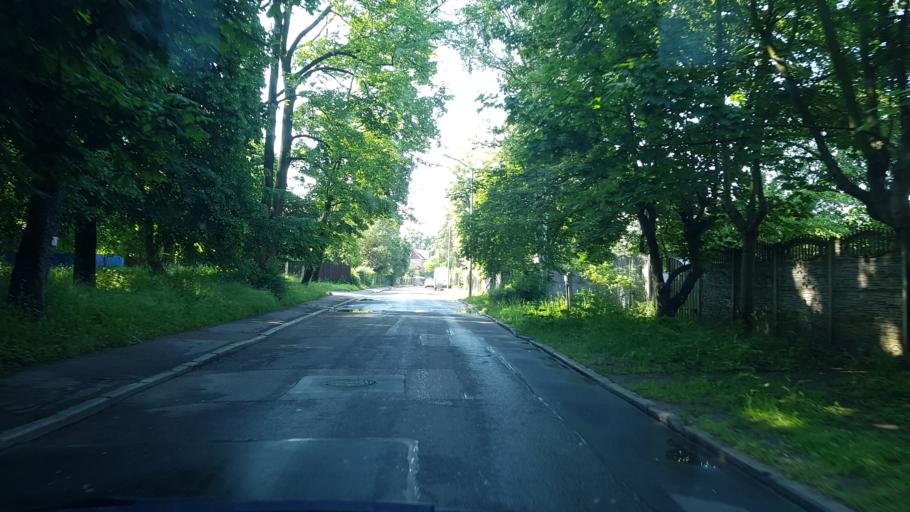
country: RU
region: Kaliningrad
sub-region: Gorod Kaliningrad
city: Kaliningrad
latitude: 54.7211
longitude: 20.4575
